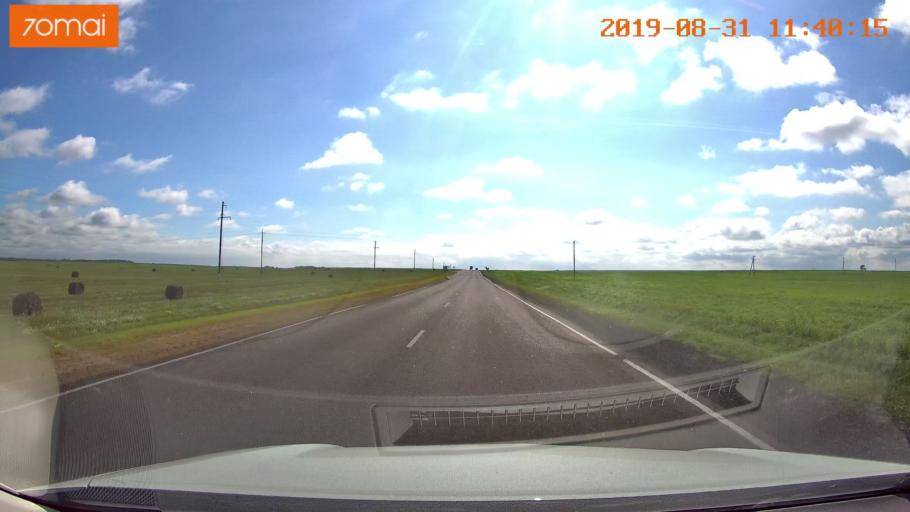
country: BY
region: Mogilev
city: Cherykaw
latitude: 53.6211
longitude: 31.2996
